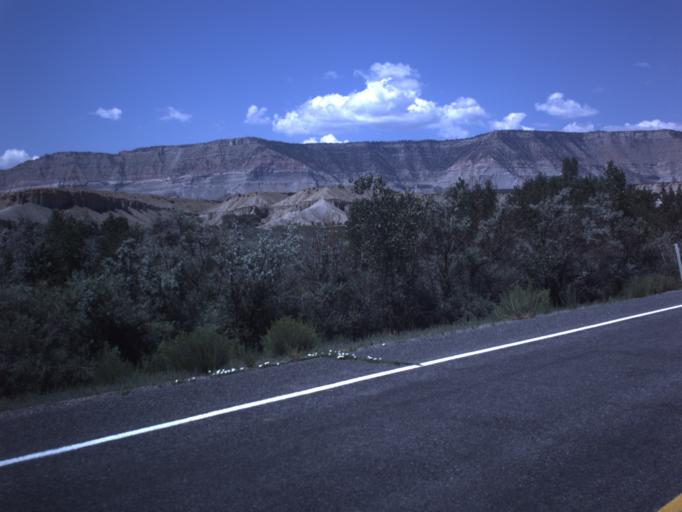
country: US
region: Utah
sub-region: Emery County
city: Orangeville
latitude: 39.2158
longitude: -111.0645
